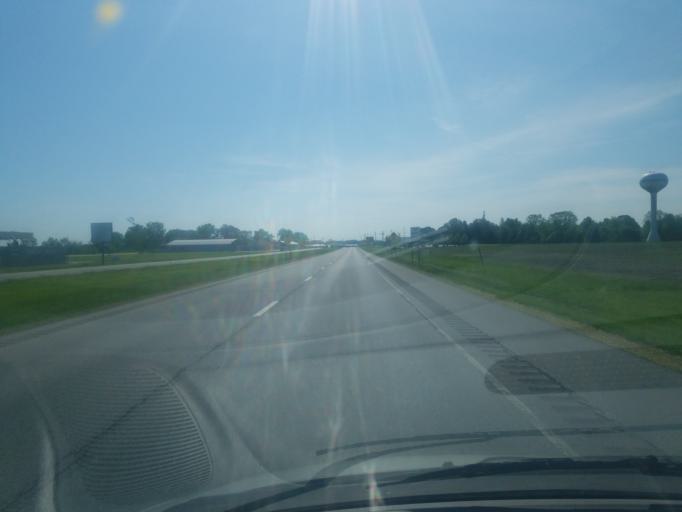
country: US
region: Ohio
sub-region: Huron County
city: Monroeville
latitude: 41.2502
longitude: -82.7098
